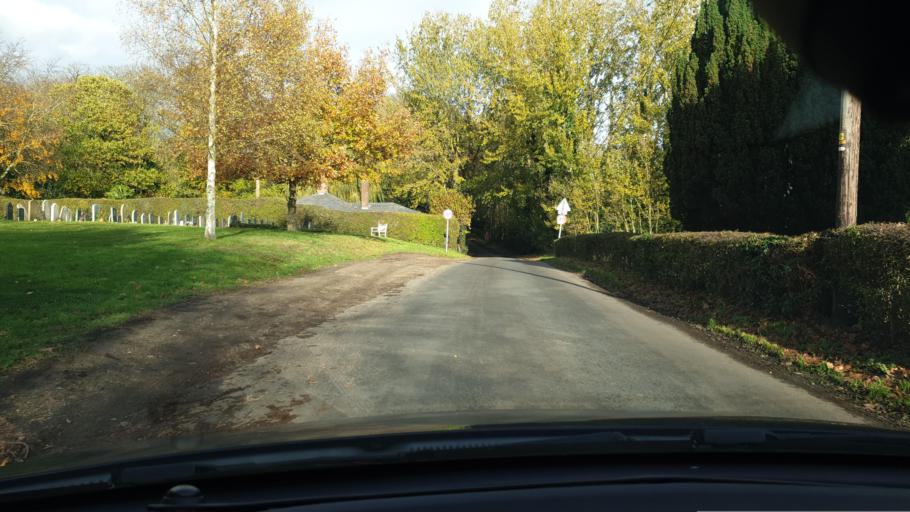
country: GB
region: England
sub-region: Essex
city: Alresford
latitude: 51.8958
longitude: 1.0275
